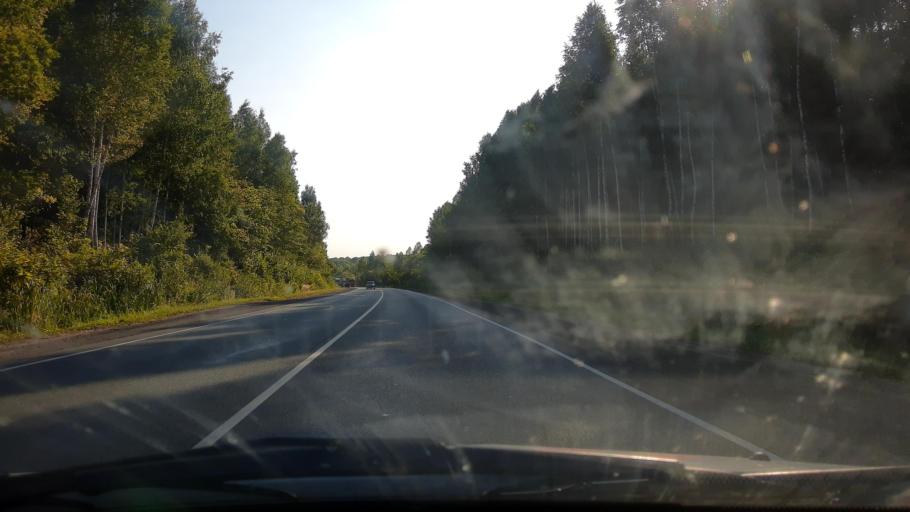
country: RU
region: Bashkortostan
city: Oktyabr'skiy
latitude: 54.4447
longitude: 53.5615
